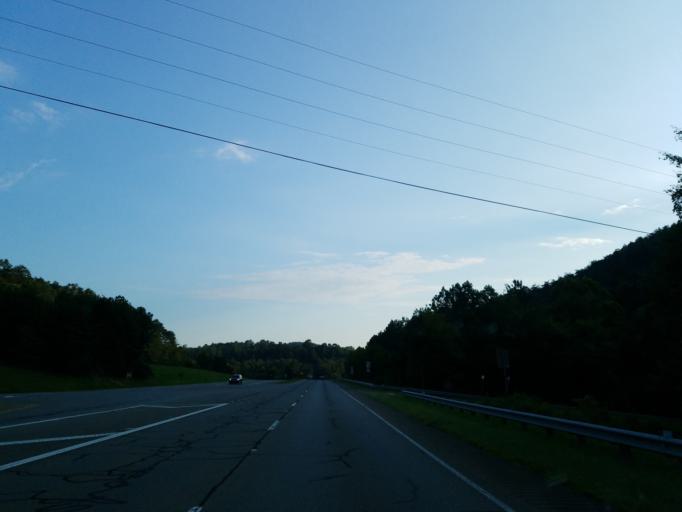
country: US
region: Georgia
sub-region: Gilmer County
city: Ellijay
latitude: 34.6925
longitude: -84.4655
